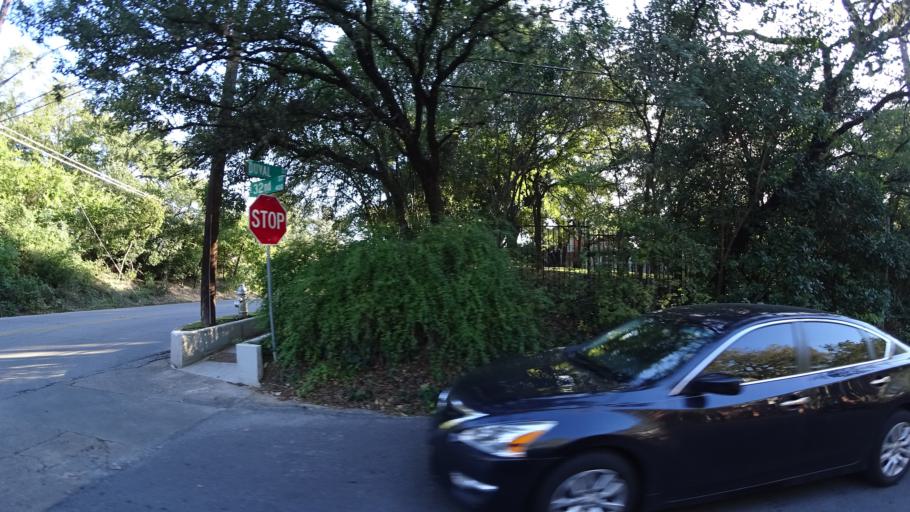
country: US
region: Texas
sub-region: Travis County
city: Austin
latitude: 30.2946
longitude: -97.7325
